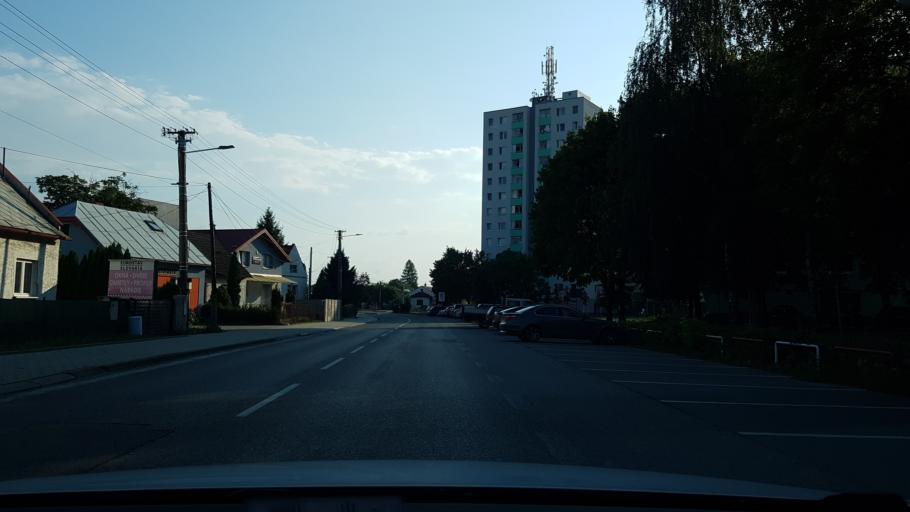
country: SK
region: Zilinsky
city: Bytca
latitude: 49.2211
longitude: 18.5547
